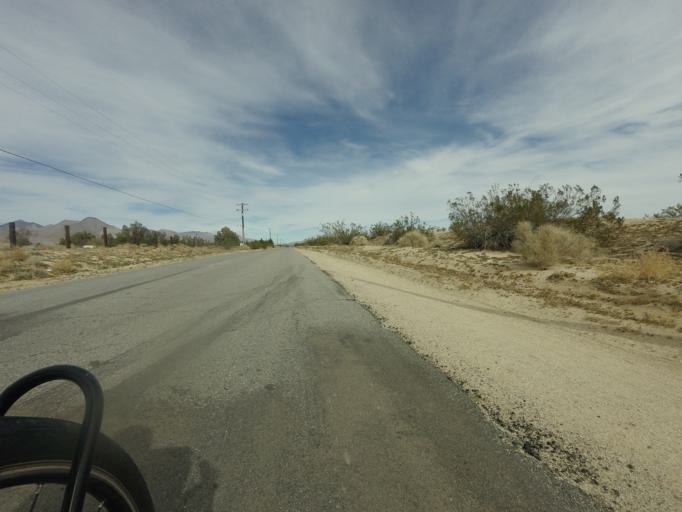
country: US
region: California
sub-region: Kern County
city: Inyokern
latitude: 35.7254
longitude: -117.8356
